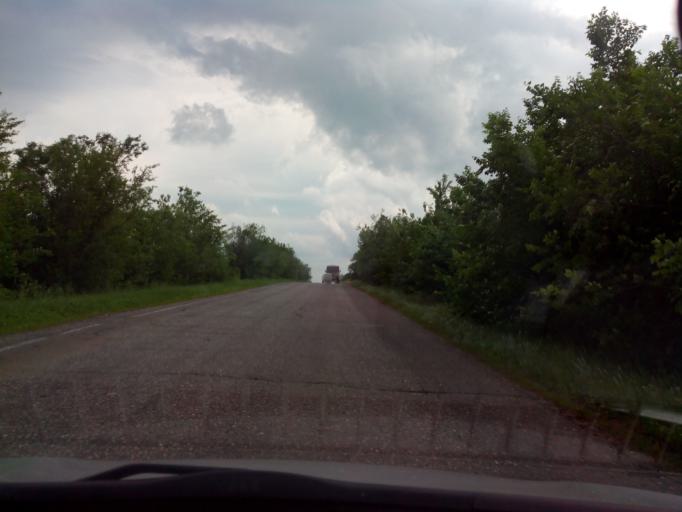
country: RU
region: Volgograd
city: Mikhaylovka
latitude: 49.9631
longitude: 43.0293
